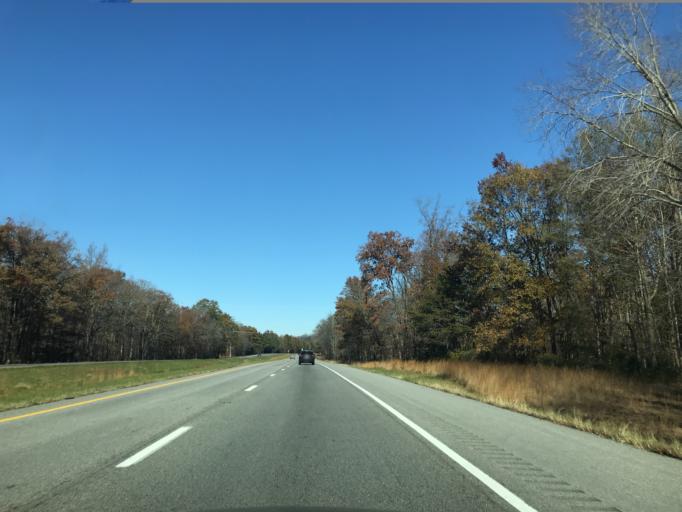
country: US
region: Maryland
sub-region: Queen Anne's County
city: Kingstown
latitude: 39.2320
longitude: -75.8748
